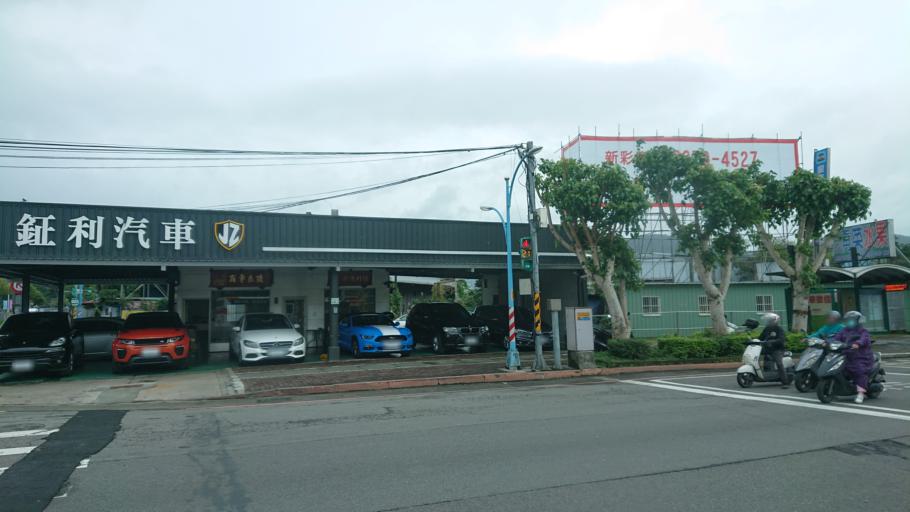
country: TW
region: Taipei
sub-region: Taipei
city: Banqiao
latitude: 24.9801
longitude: 121.4525
